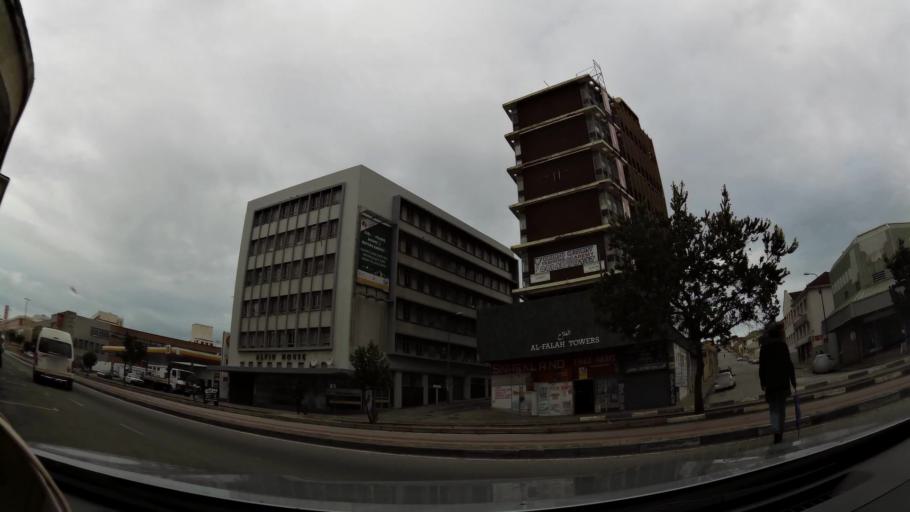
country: ZA
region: Eastern Cape
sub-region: Nelson Mandela Bay Metropolitan Municipality
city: Port Elizabeth
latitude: -33.9480
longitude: 25.6067
